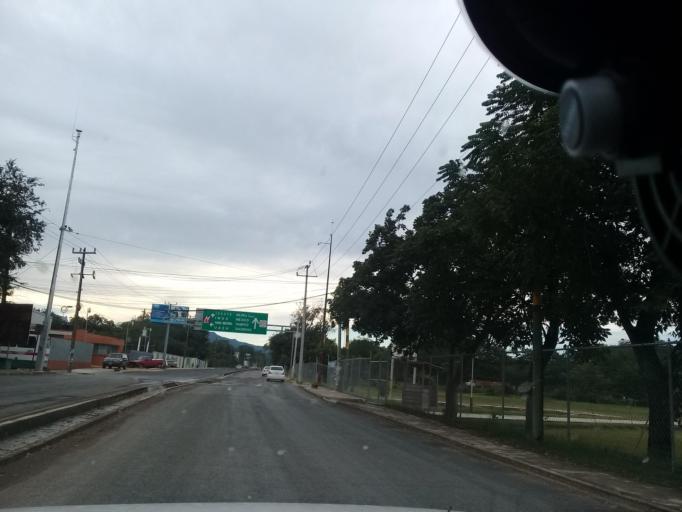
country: MX
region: Hidalgo
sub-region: Huejutla de Reyes
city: Parque de Poblamiento Solidaridad
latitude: 21.1538
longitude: -98.3869
